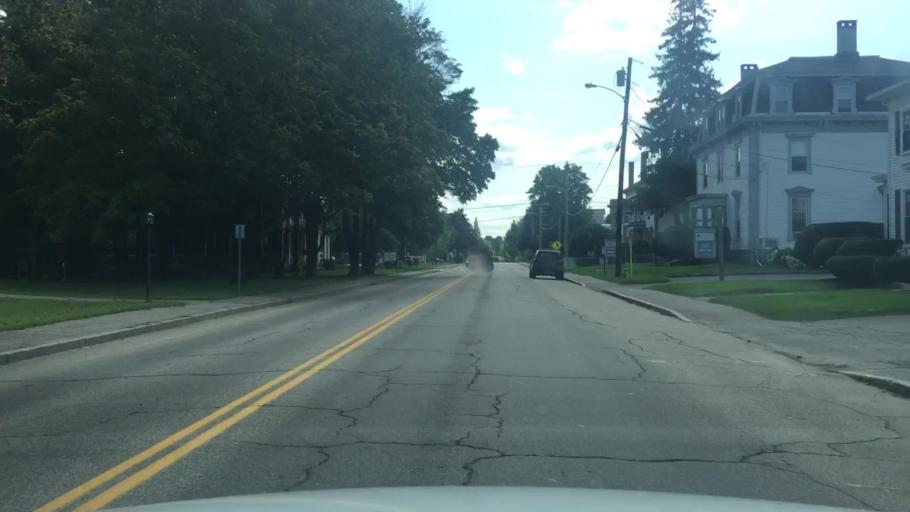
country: US
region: Maine
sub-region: Kennebec County
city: Augusta
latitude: 44.3136
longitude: -69.7782
